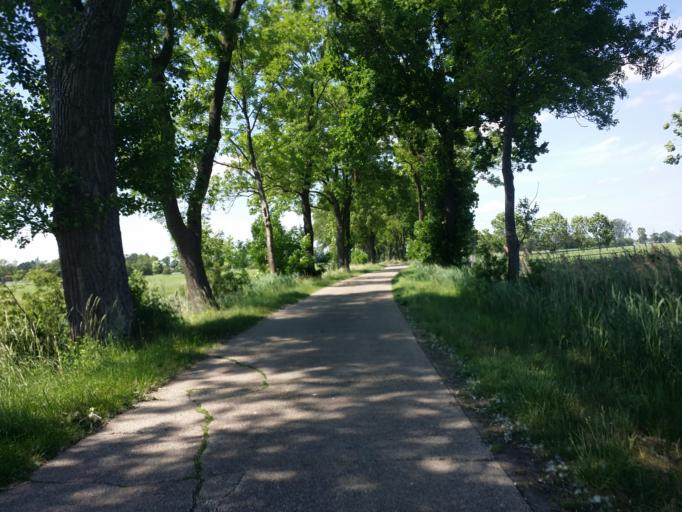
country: DE
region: Lower Saxony
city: Neuenkirchen
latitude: 53.1667
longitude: 8.5100
